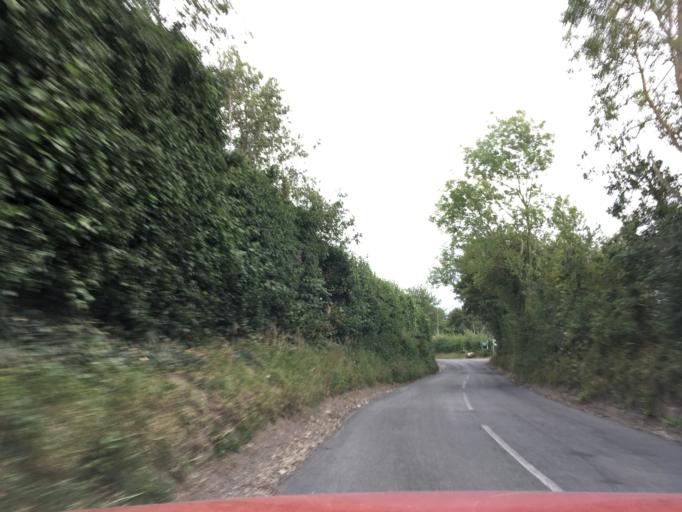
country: GB
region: England
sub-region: Kent
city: Yalding
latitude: 51.2390
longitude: 0.4482
